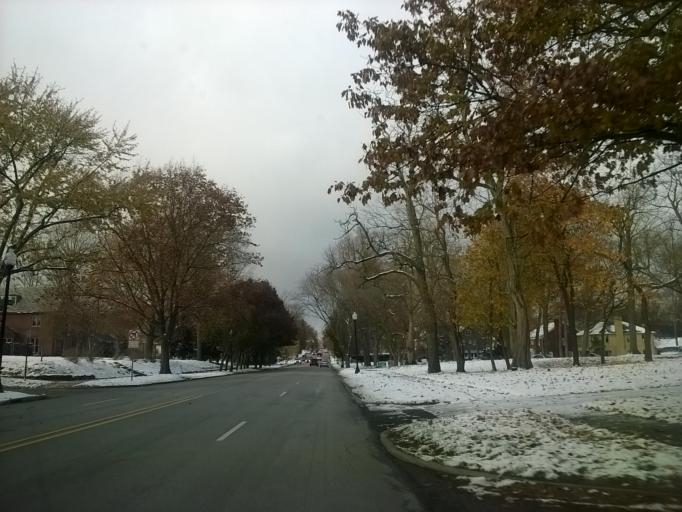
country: US
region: Indiana
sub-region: Marion County
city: Broad Ripple
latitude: 39.8364
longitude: -86.1569
